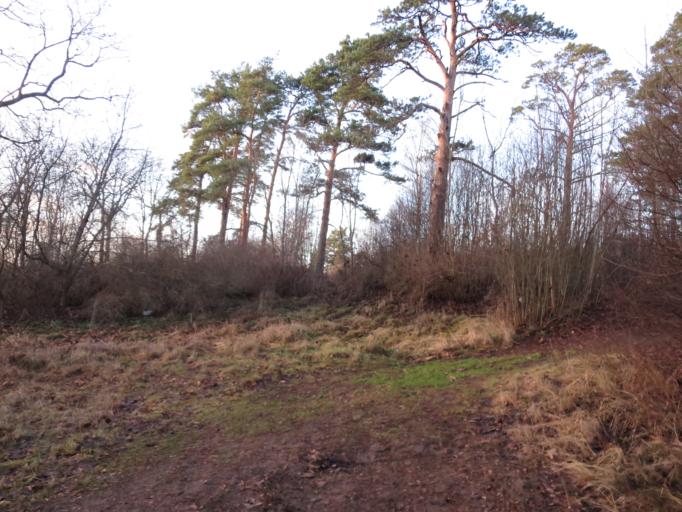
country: LV
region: Riga
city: Bergi
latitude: 56.9730
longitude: 24.3080
